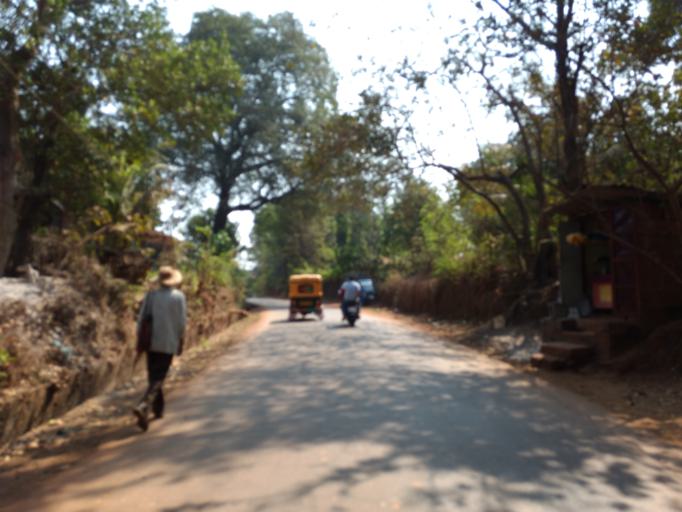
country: IN
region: Maharashtra
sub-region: Sindhudurg
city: Kudal
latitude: 16.0144
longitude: 73.6841
